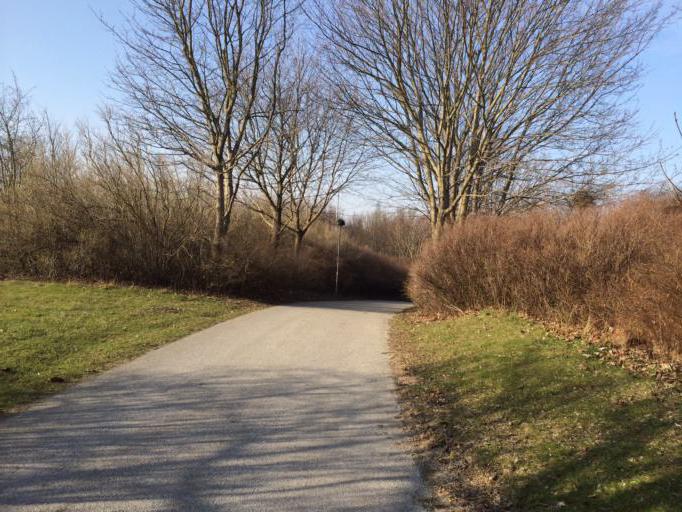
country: SE
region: Skane
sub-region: Lunds Kommun
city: Lund
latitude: 55.7168
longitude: 13.1683
